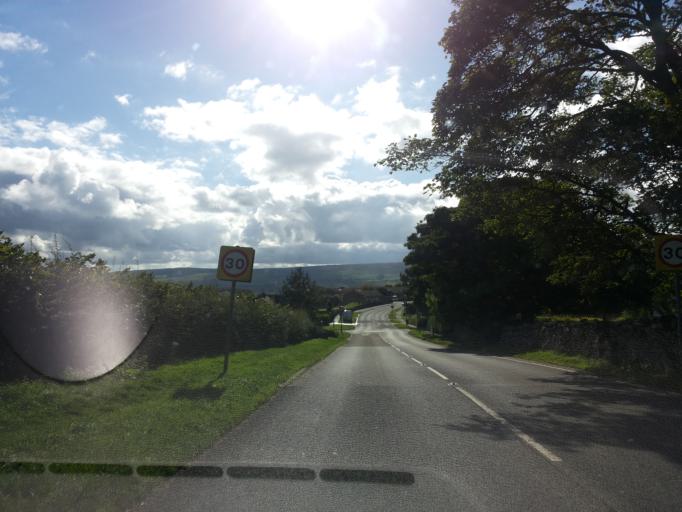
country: GB
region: England
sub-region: North Yorkshire
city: Leyburn
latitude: 54.3165
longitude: -1.8235
